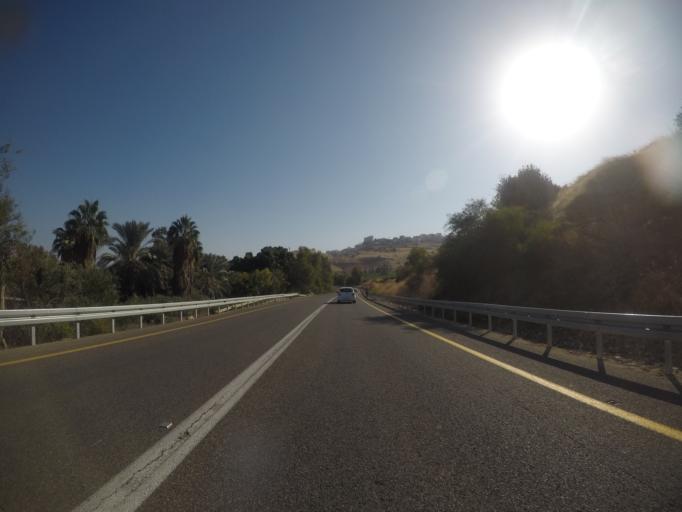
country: IL
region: Northern District
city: Tiberias
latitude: 32.8123
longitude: 35.5220
